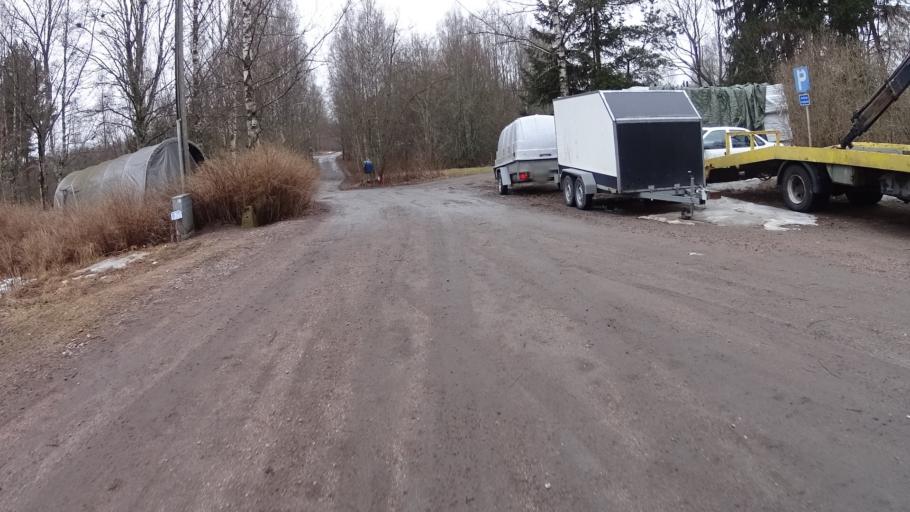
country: FI
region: Uusimaa
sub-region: Helsinki
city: Kilo
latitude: 60.2615
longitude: 24.7927
